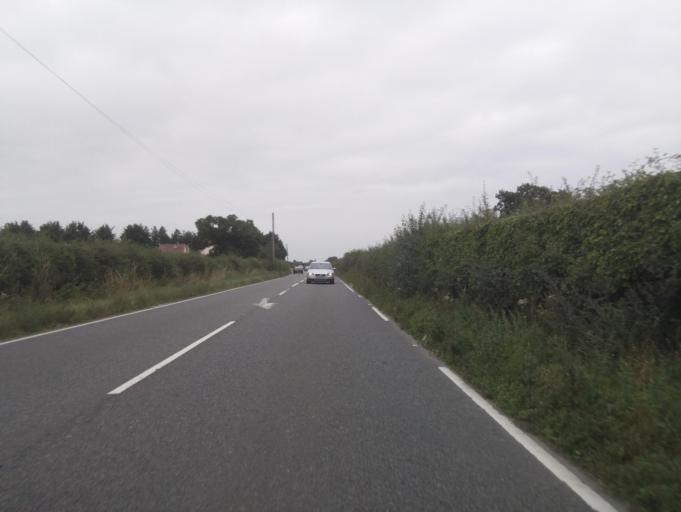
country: GB
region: England
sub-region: Shropshire
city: Astley
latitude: 52.7497
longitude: -2.7032
